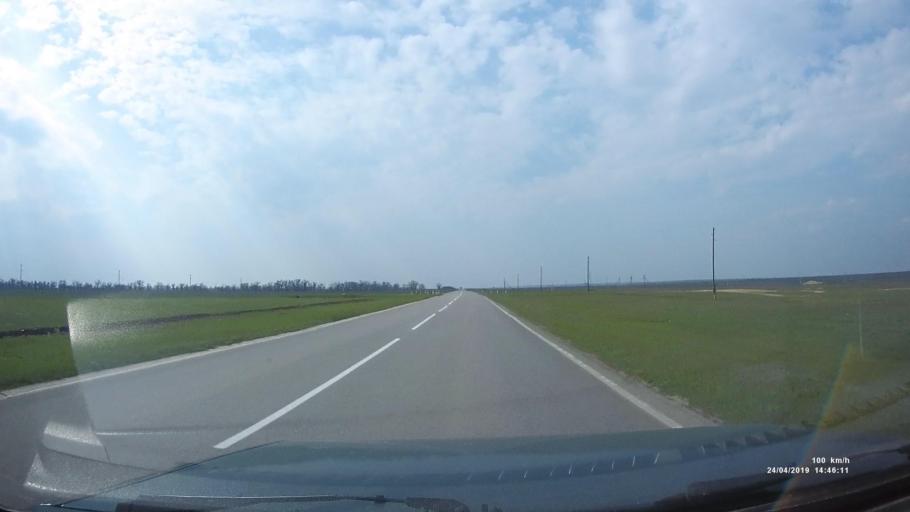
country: RU
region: Rostov
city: Remontnoye
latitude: 46.4801
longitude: 43.7938
